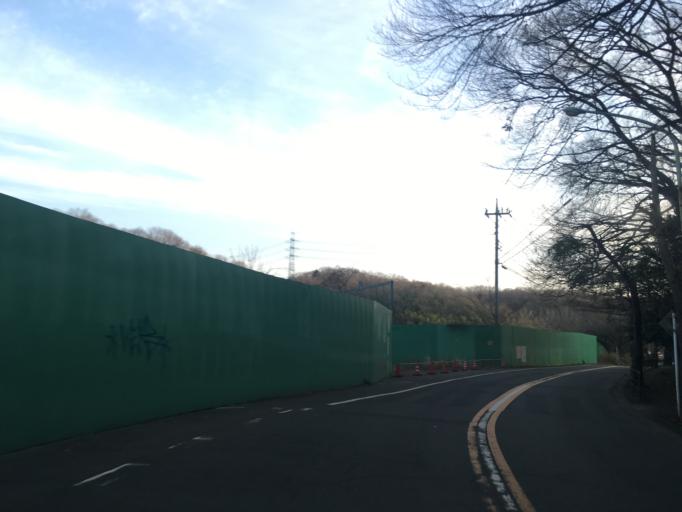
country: JP
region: Tokyo
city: Hino
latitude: 35.6418
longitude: 139.3938
